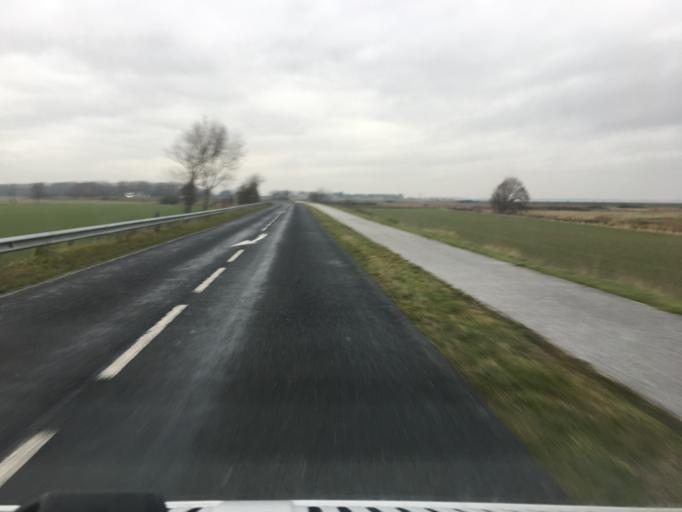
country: FR
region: Picardie
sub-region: Departement de la Somme
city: Pende
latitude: 50.2032
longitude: 1.5564
